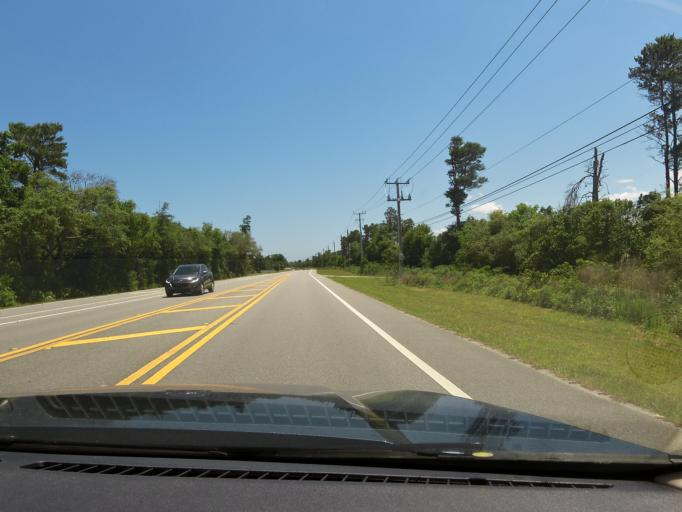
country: US
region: Florida
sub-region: Flagler County
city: Flagler Beach
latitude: 29.4387
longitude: -81.1586
